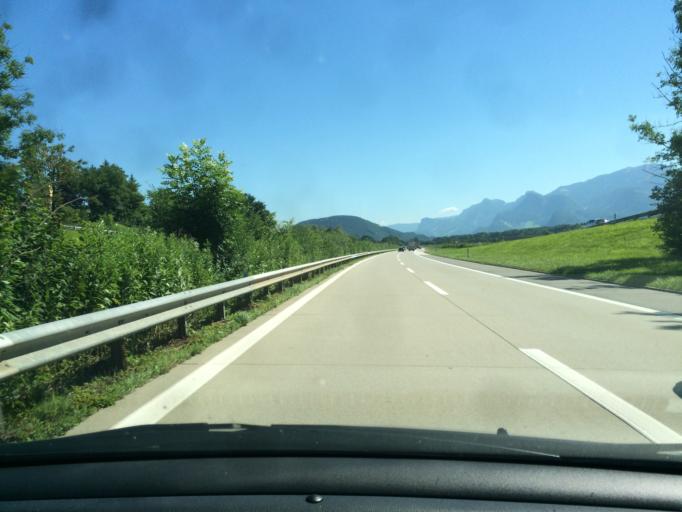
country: CH
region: Saint Gallen
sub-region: Wahlkreis Rheintal
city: Oberriet
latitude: 47.3082
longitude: 9.5693
